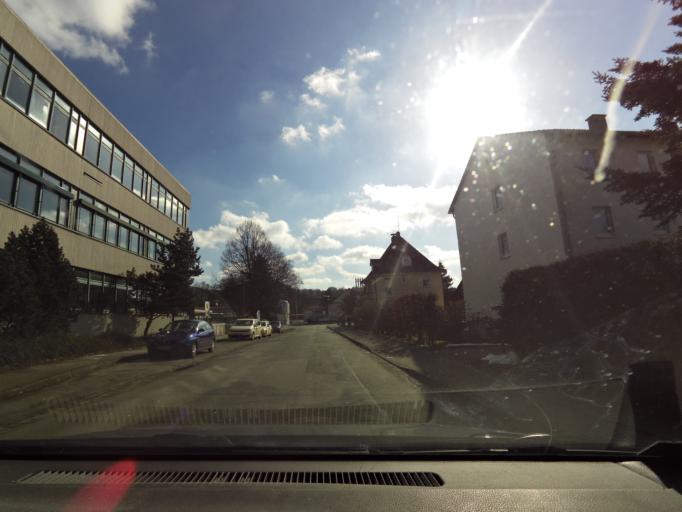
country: DE
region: Lower Saxony
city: Bad Lauterberg im Harz
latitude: 51.6265
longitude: 10.4624
